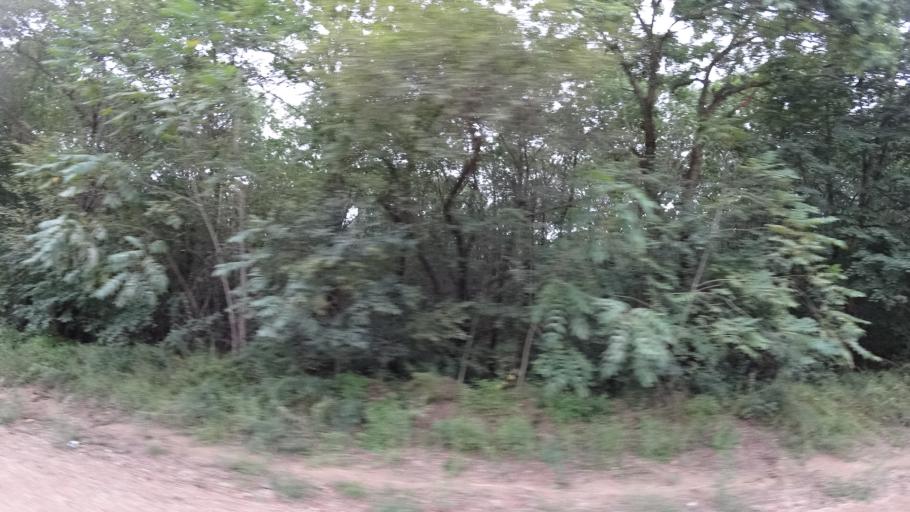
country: RU
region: Primorskiy
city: Rettikhovka
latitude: 44.2499
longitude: 132.6961
